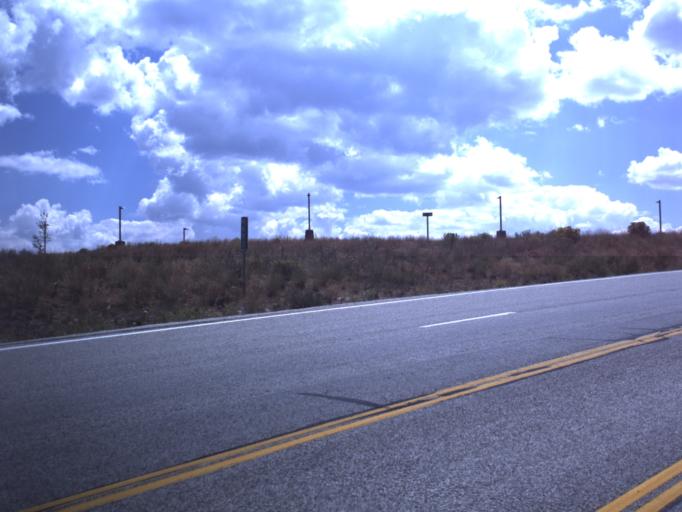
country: US
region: Idaho
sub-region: Bear Lake County
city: Paris
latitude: 41.9224
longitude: -111.4578
